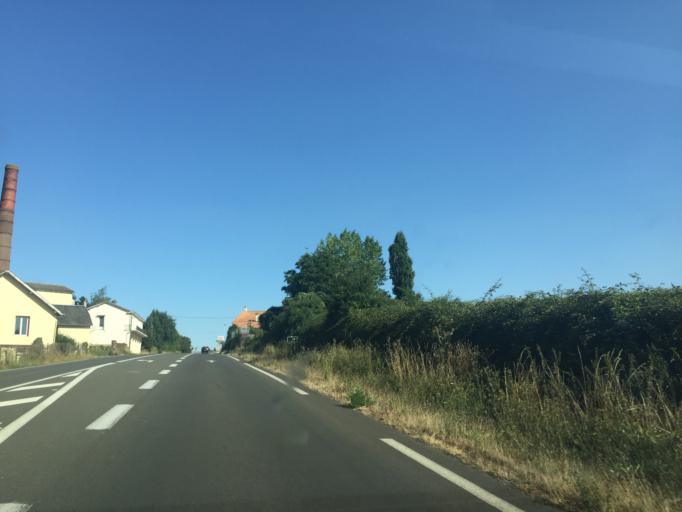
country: FR
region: Poitou-Charentes
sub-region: Departement des Deux-Sevres
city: Melle
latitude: 46.2057
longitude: -0.0990
